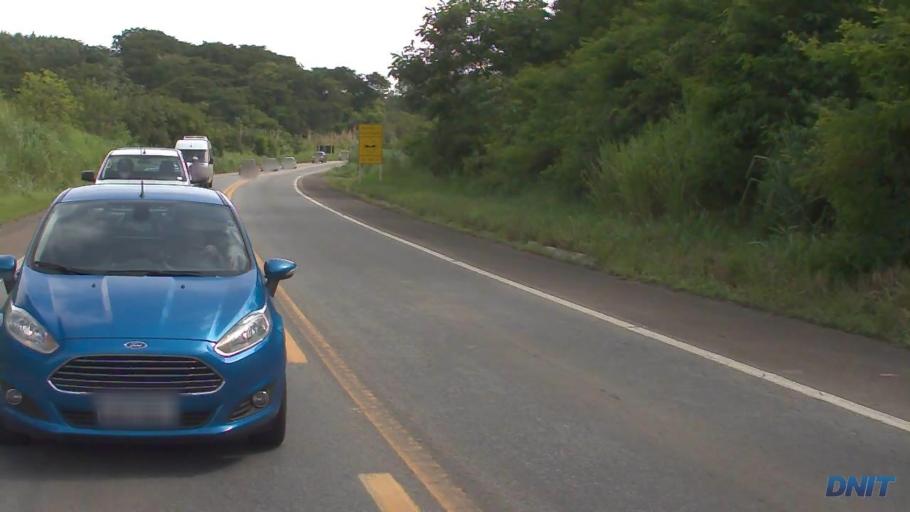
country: BR
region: Minas Gerais
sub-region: Ipaba
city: Ipaba
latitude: -19.3600
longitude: -42.4395
